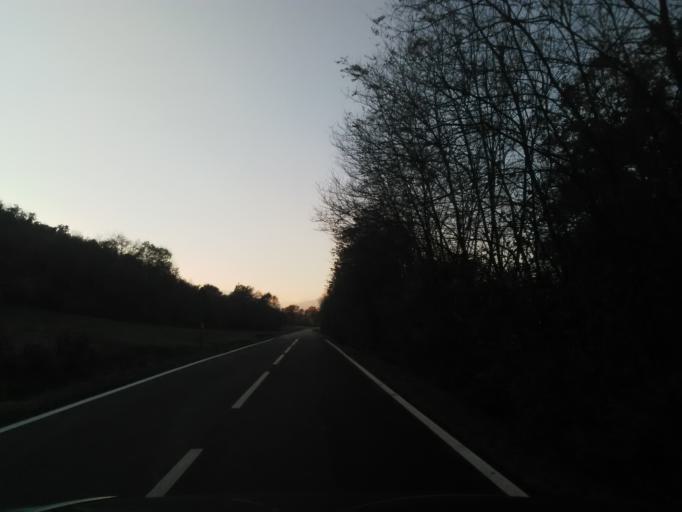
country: IT
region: Piedmont
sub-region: Provincia di Biella
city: Salussola
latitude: 45.4545
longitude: 8.0919
